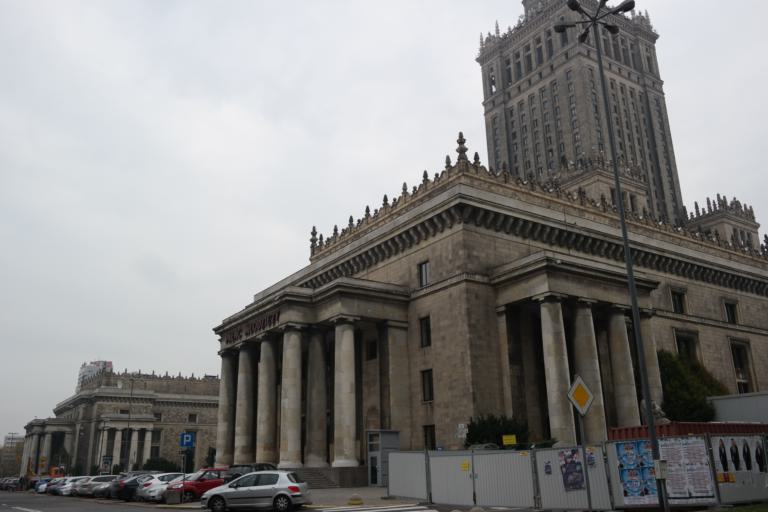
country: PL
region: Masovian Voivodeship
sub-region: Warszawa
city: Warsaw
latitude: 52.2330
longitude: 21.0044
